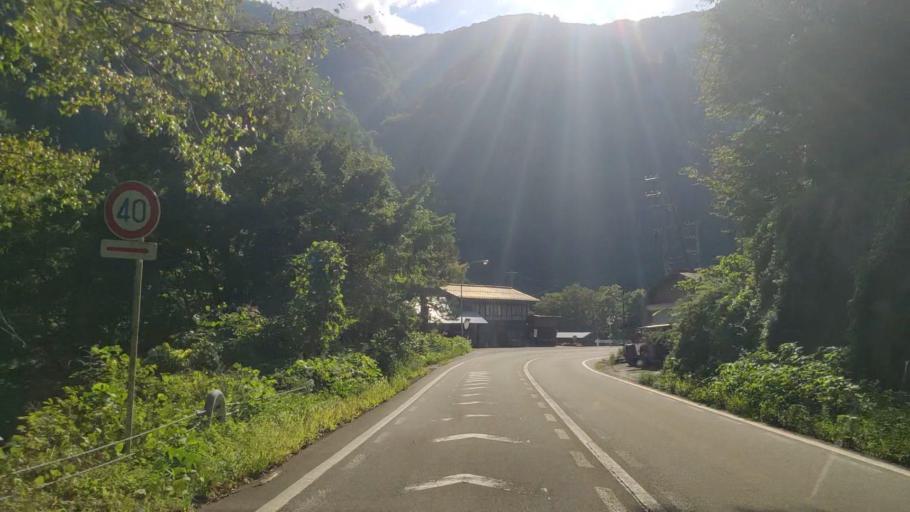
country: JP
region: Gifu
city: Takayama
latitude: 36.2955
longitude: 137.1184
